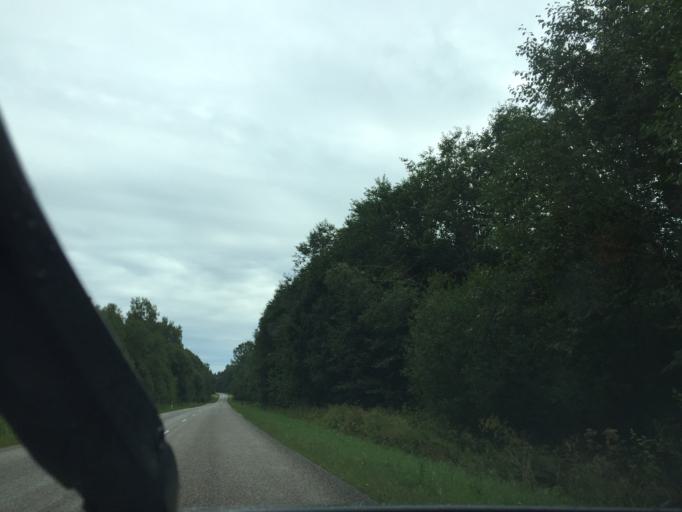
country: LV
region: Dagda
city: Dagda
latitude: 56.1953
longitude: 27.3332
